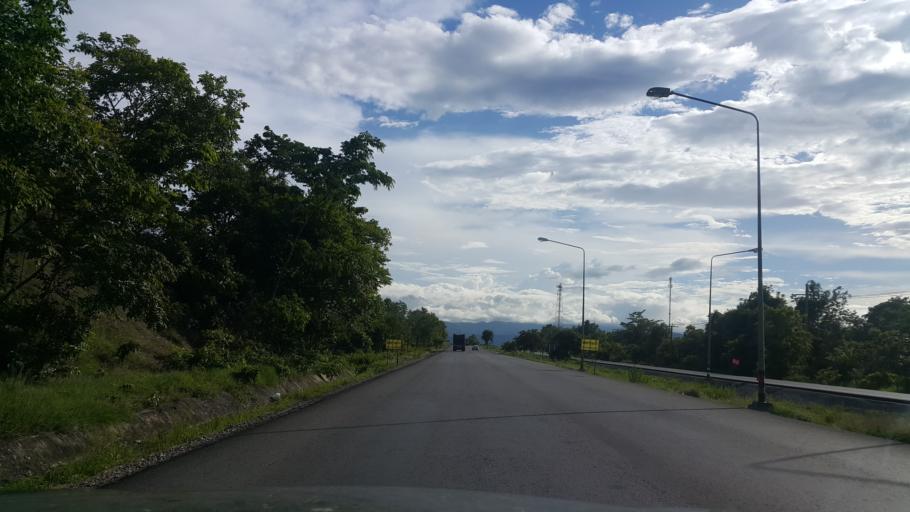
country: TH
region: Tak
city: Ban Tak
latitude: 17.1382
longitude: 99.1128
